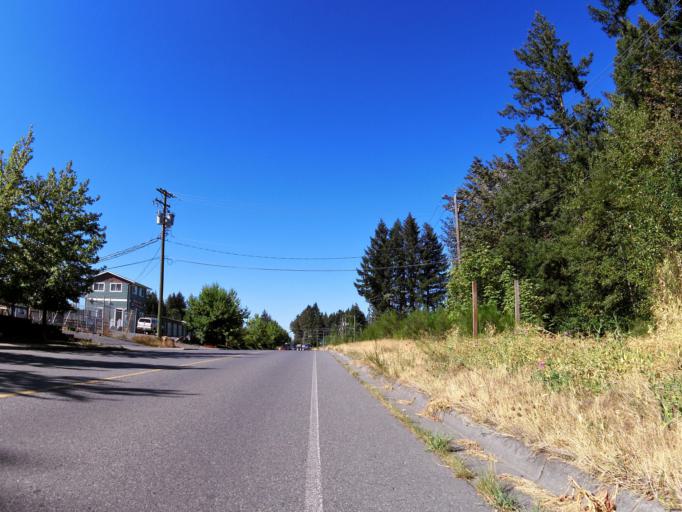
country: CA
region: British Columbia
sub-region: Cowichan Valley Regional District
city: Ladysmith
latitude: 49.0026
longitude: -123.8303
